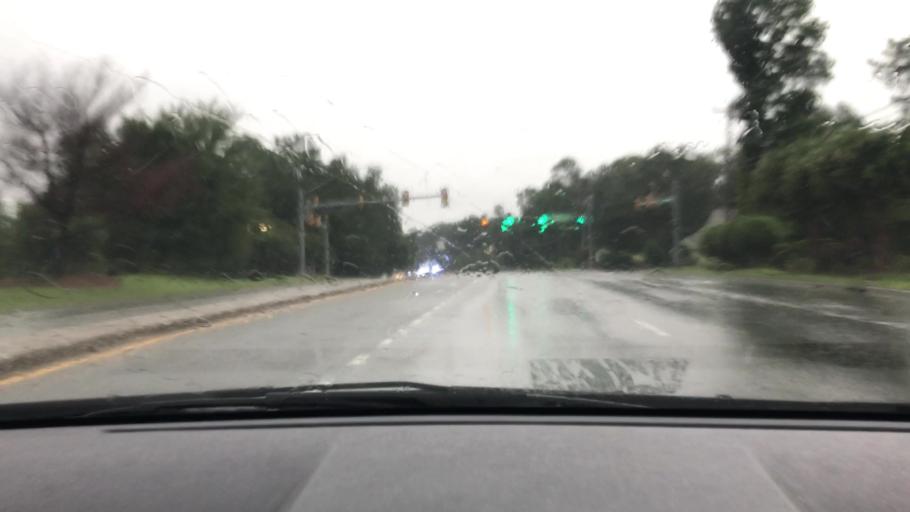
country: US
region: Virginia
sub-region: Henrico County
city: Short Pump
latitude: 37.6640
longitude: -77.5697
